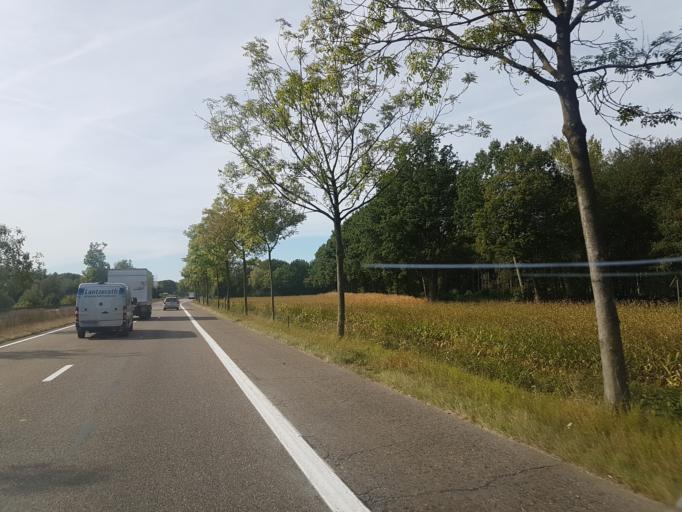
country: BE
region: Flanders
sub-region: Provincie Antwerpen
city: Mol
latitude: 51.1708
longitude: 5.0873
